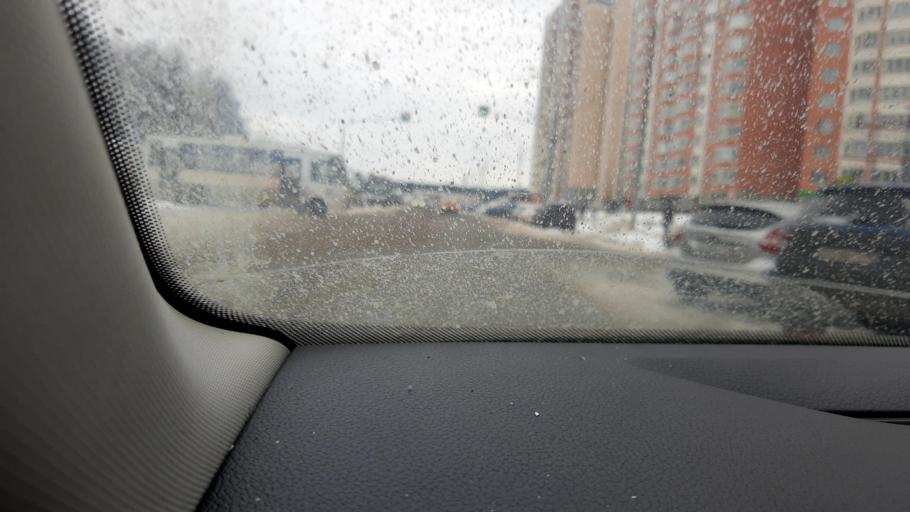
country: RU
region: Moskovskaya
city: Shcherbinka
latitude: 55.5240
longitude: 37.6035
